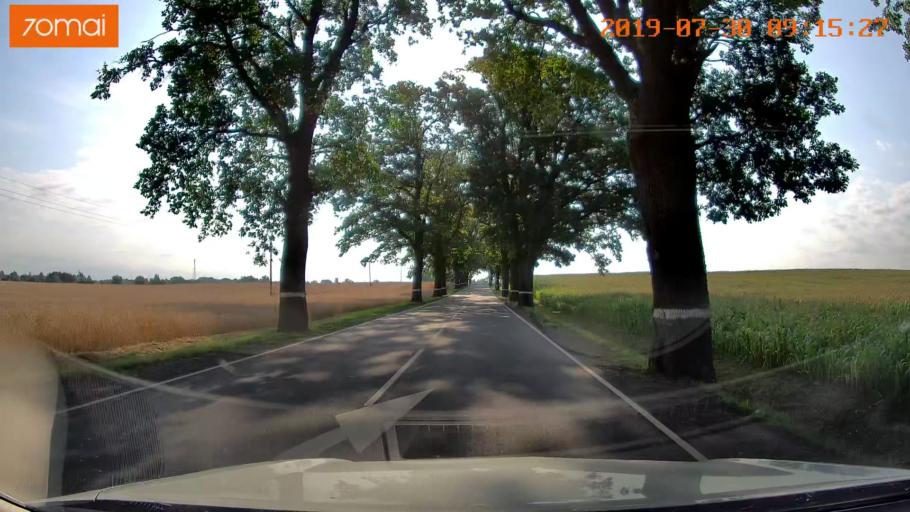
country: RU
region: Kaliningrad
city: Nesterov
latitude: 54.6337
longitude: 22.5403
